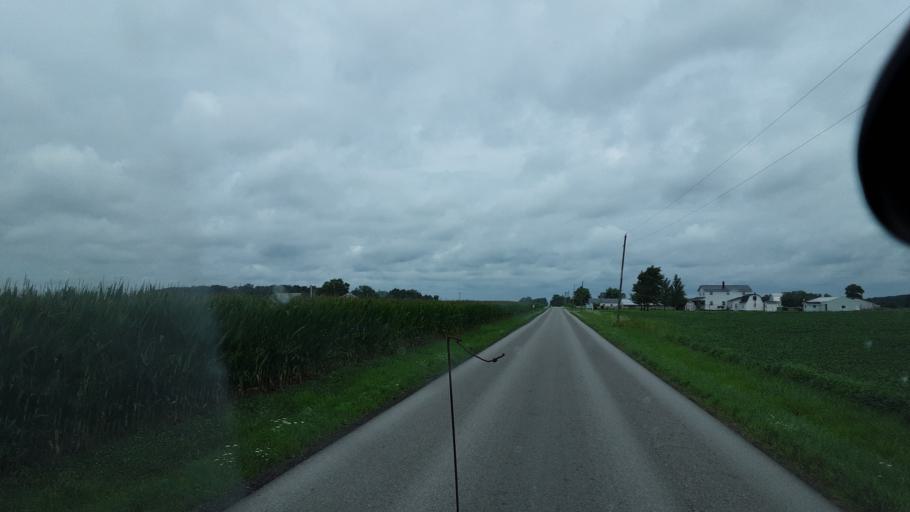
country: US
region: Indiana
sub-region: Adams County
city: Berne
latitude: 40.7245
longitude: -84.9944
